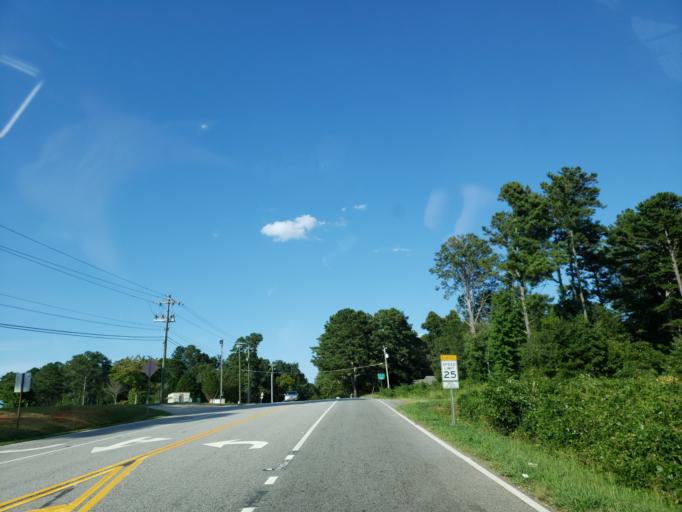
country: US
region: Georgia
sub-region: Forsyth County
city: Cumming
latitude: 34.2396
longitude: -84.1757
